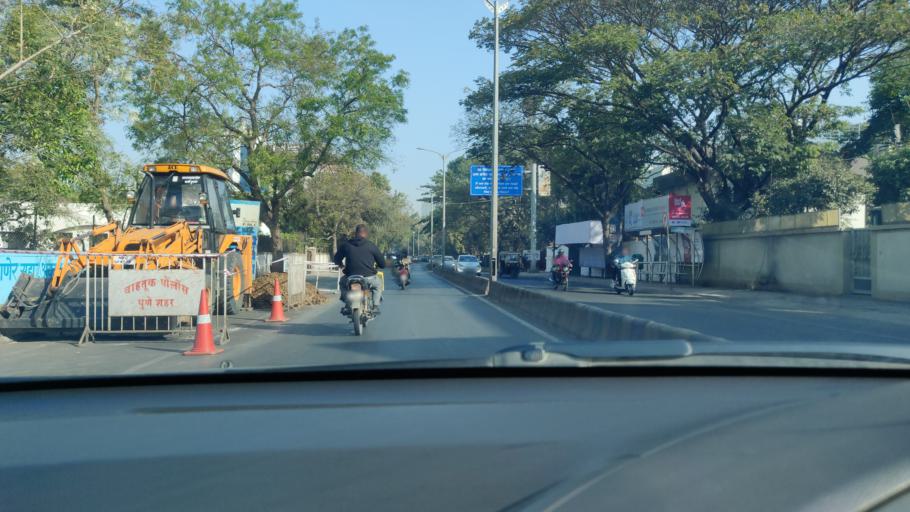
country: IN
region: Maharashtra
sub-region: Pune Division
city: Khadki
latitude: 18.5511
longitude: 73.8096
